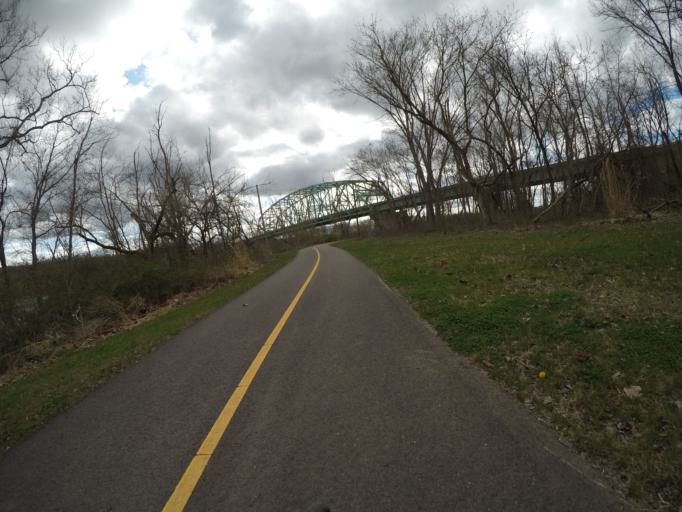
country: US
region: West Virginia
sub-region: Wood County
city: Williamstown
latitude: 39.4057
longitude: -81.4270
